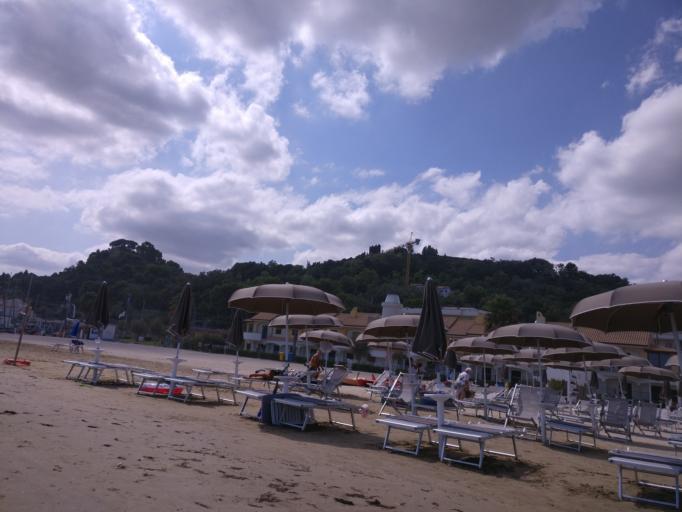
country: IT
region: The Marches
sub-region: Provincia di Ascoli Piceno
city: Cupra Marittima
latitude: 43.0219
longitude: 13.8622
